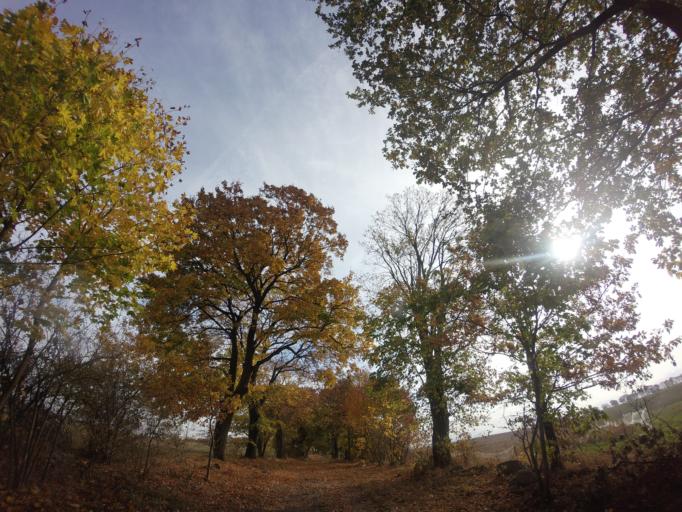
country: PL
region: West Pomeranian Voivodeship
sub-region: Powiat choszczenski
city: Recz
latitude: 53.2632
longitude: 15.6245
